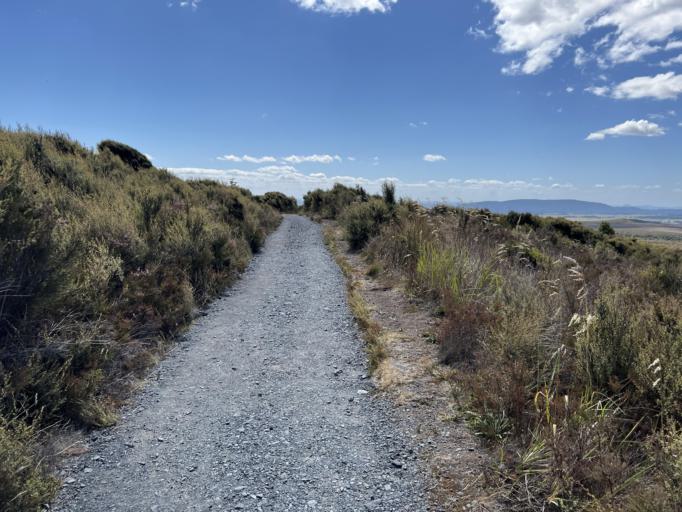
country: NZ
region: Manawatu-Wanganui
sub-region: Ruapehu District
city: Waiouru
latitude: -39.1997
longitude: 175.5458
